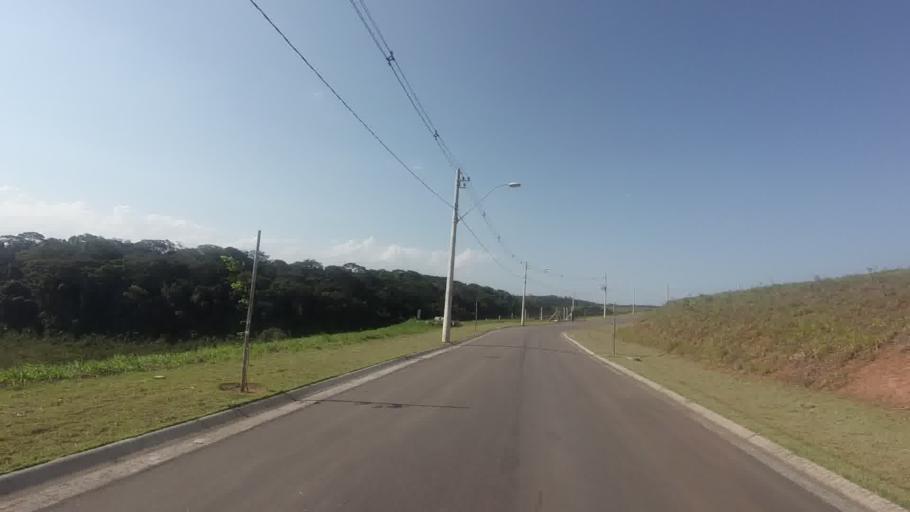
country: BR
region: Espirito Santo
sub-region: Guarapari
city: Guarapari
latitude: -20.7117
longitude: -40.5318
